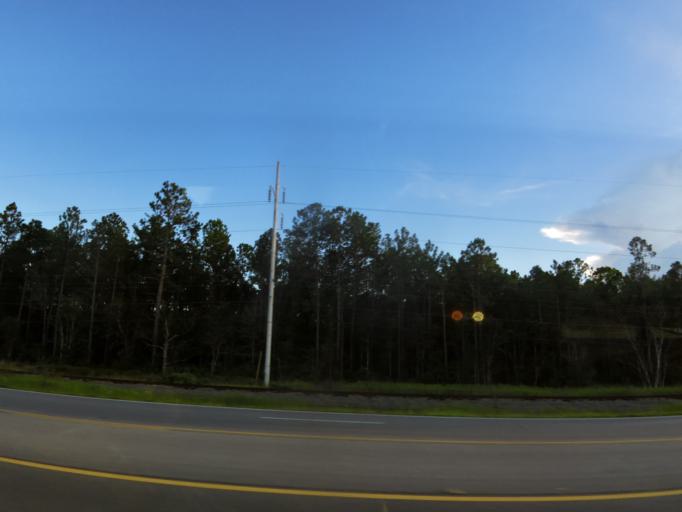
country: US
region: Georgia
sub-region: Camden County
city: Kingsland
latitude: 30.7829
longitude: -81.6339
